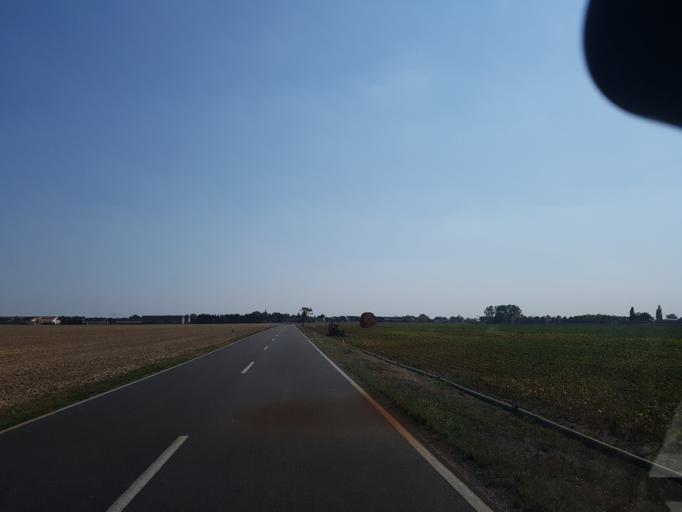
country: DE
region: Saxony-Anhalt
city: Prettin
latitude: 51.6553
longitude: 12.9869
